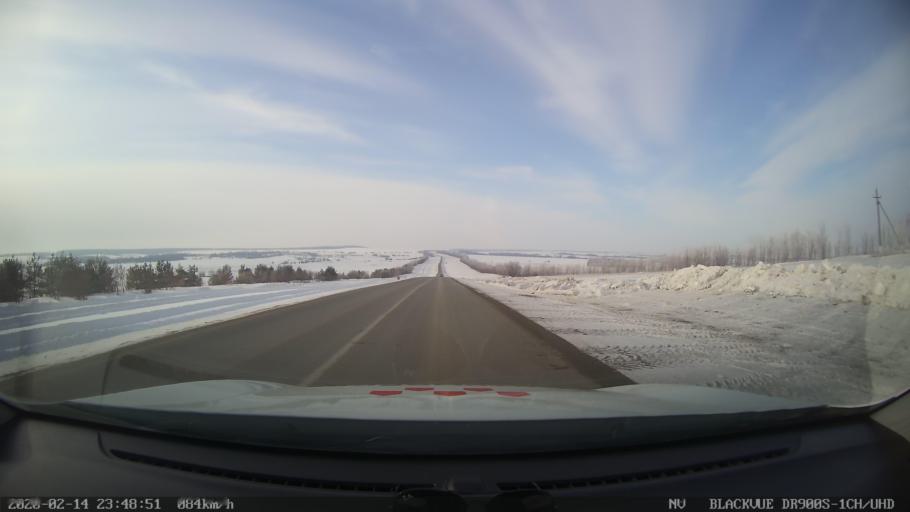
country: RU
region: Tatarstan
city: Kuybyshevskiy Zaton
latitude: 55.2499
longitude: 49.1950
